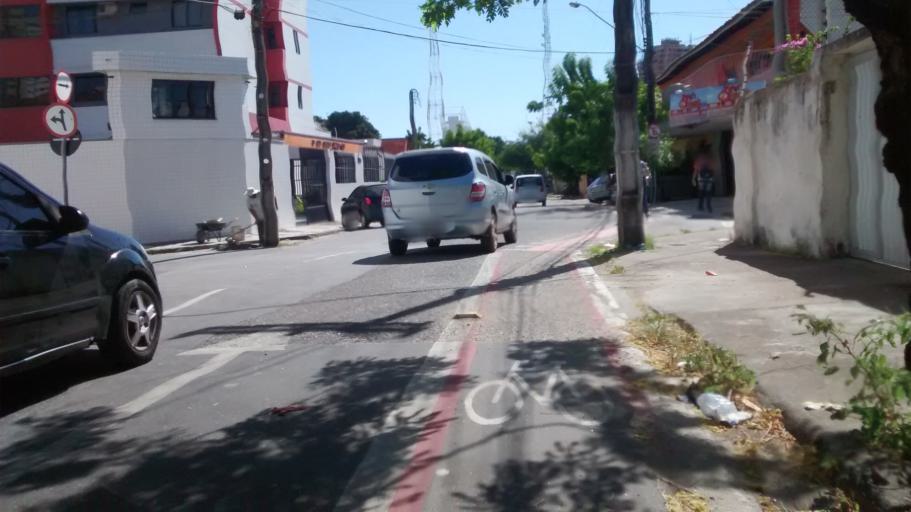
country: BR
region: Ceara
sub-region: Fortaleza
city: Fortaleza
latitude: -3.7413
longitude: -38.5136
